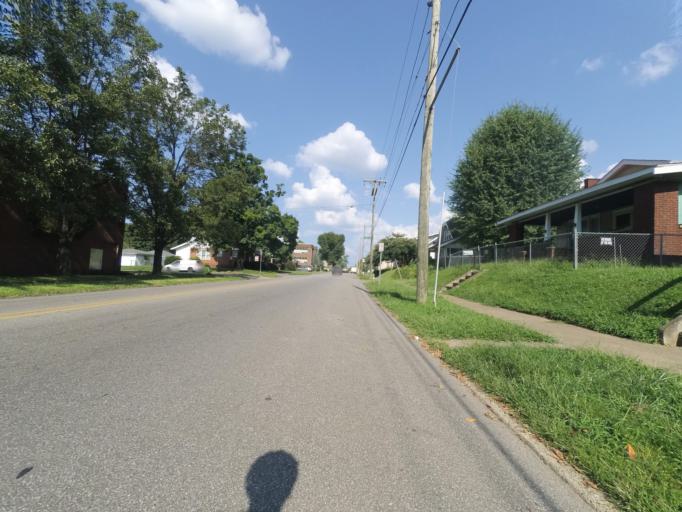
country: US
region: West Virginia
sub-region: Cabell County
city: Huntington
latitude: 38.4131
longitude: -82.4616
